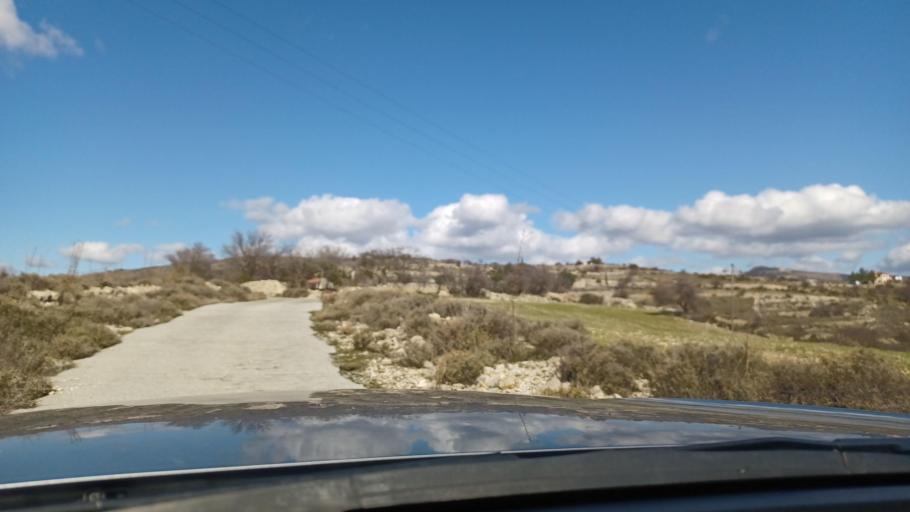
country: CY
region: Limassol
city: Pachna
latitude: 34.8260
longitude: 32.7944
